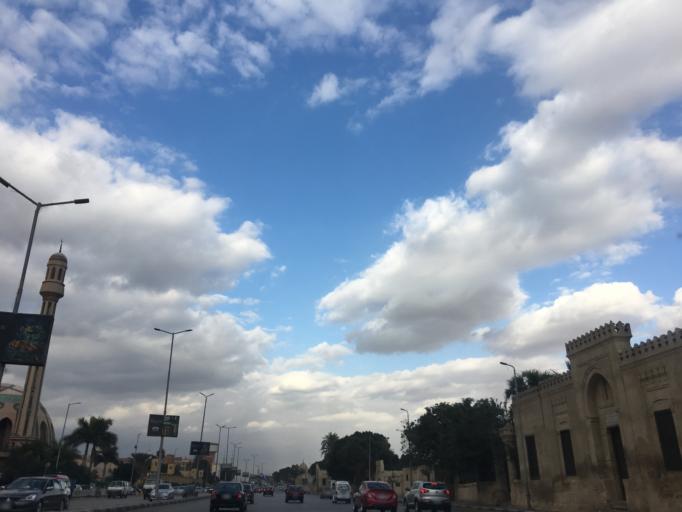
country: EG
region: Muhafazat al Qahirah
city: Cairo
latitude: 30.0509
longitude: 31.2759
